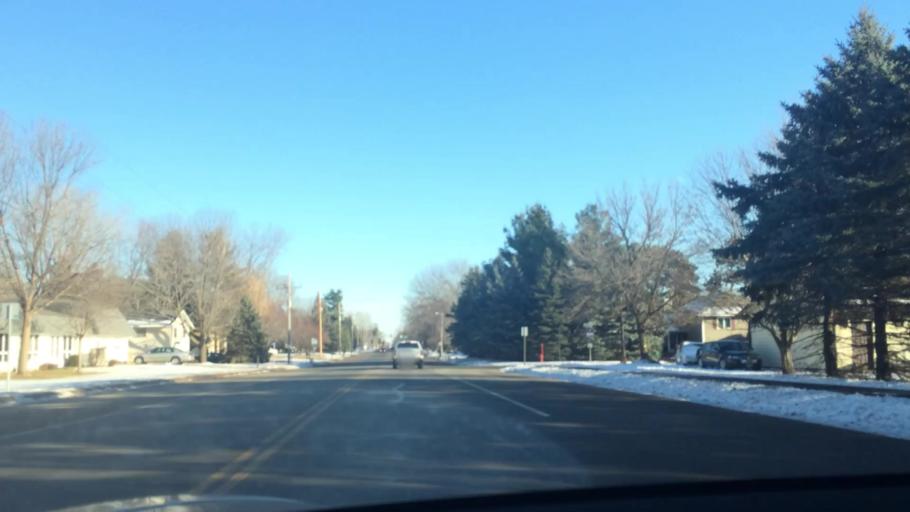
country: US
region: Minnesota
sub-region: Anoka County
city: Circle Pines
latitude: 45.1242
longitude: -93.1333
